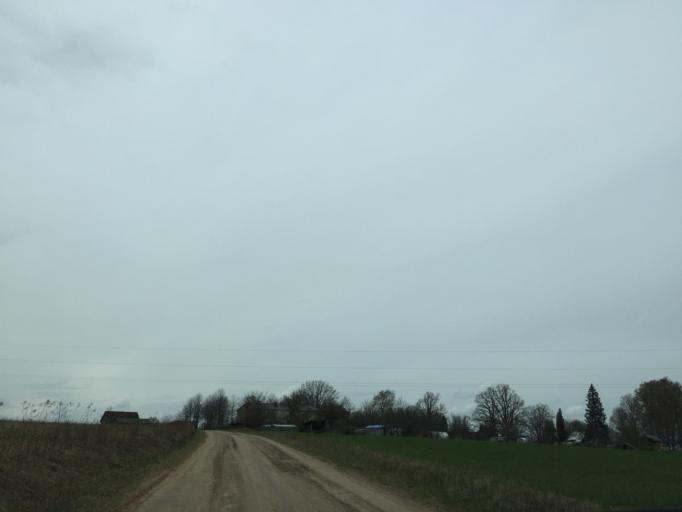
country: LV
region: Priekuli
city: Priekuli
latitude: 57.3372
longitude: 25.3728
